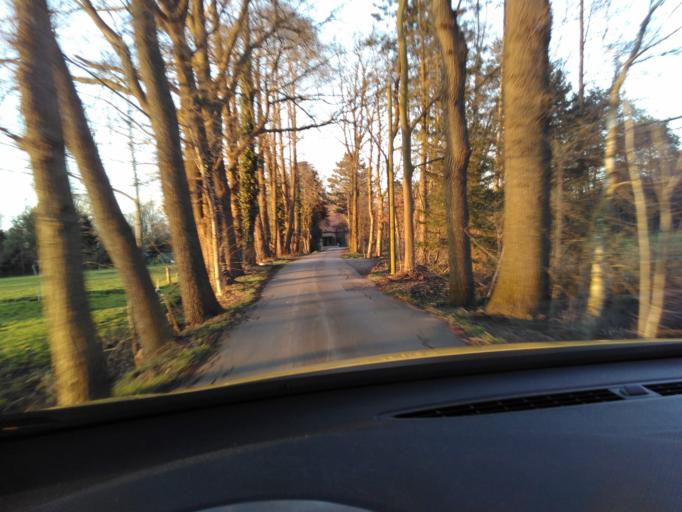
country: DE
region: North Rhine-Westphalia
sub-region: Regierungsbezirk Detmold
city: Verl
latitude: 51.8835
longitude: 8.5217
